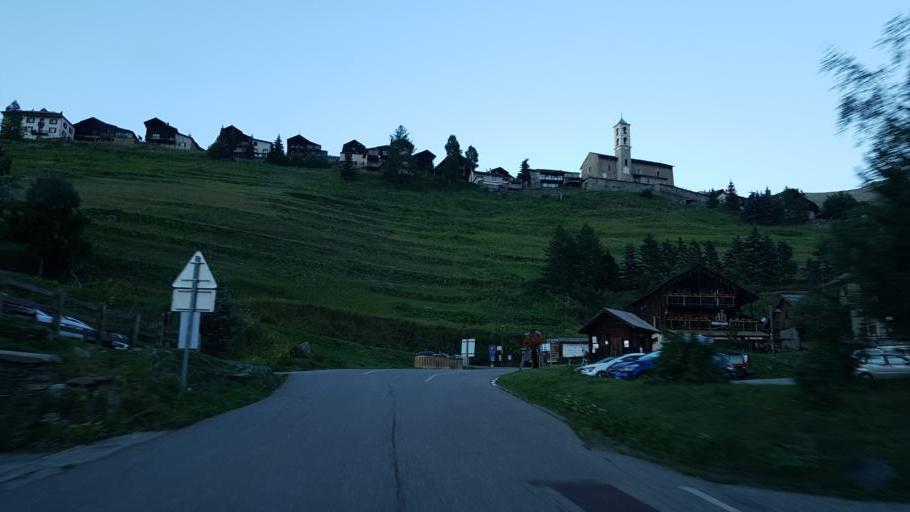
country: IT
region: Piedmont
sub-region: Provincia di Cuneo
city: Pontechianale
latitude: 44.6994
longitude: 6.8651
